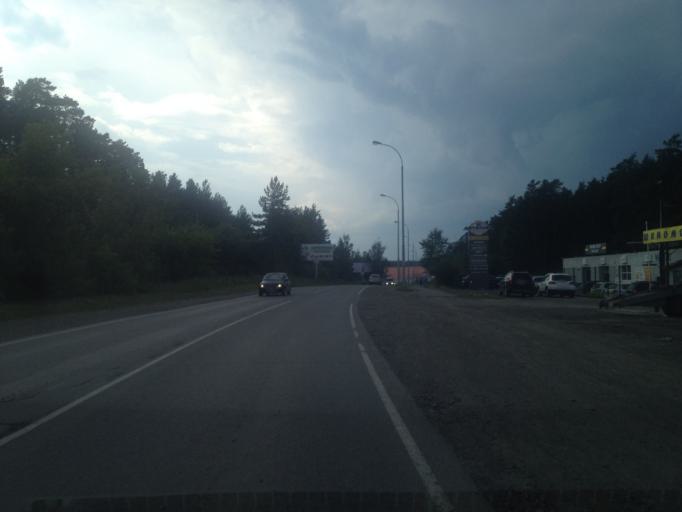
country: RU
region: Sverdlovsk
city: Shirokaya Rechka
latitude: 56.8180
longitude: 60.5122
